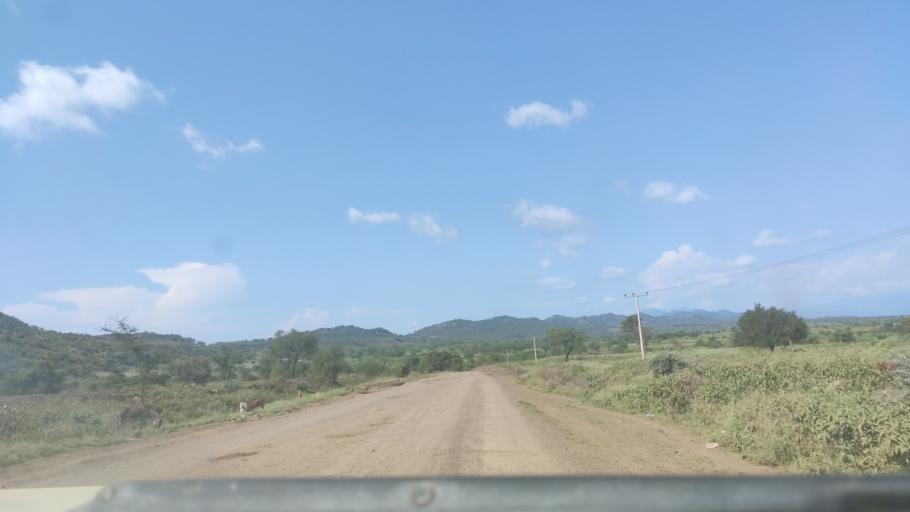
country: ET
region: Southern Nations, Nationalities, and People's Region
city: Felege Neway
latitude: 6.3725
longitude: 37.0866
